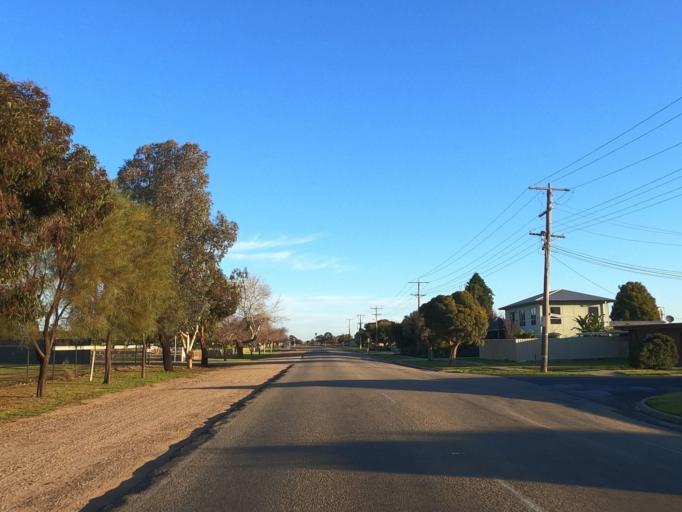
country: AU
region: Victoria
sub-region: Swan Hill
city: Swan Hill
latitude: -35.3522
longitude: 143.5536
